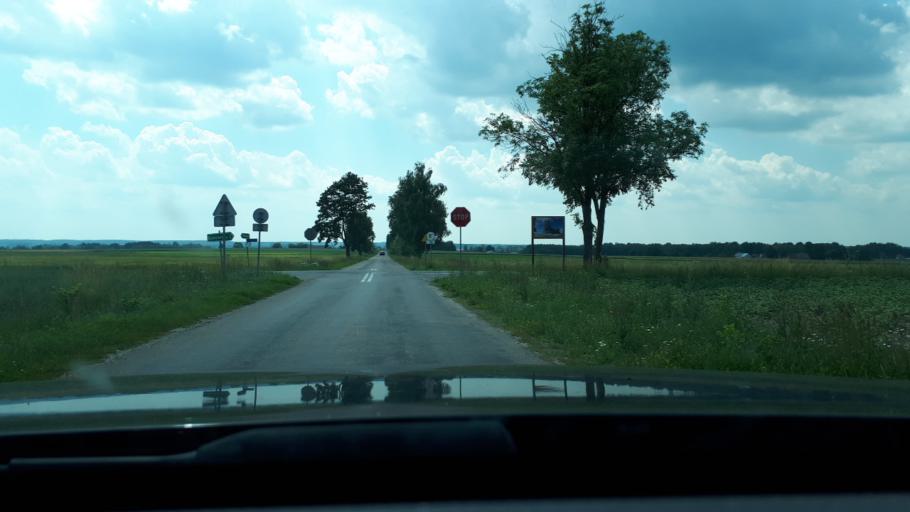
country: PL
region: Podlasie
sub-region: Powiat bialostocki
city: Lapy
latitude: 53.0957
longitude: 22.8563
